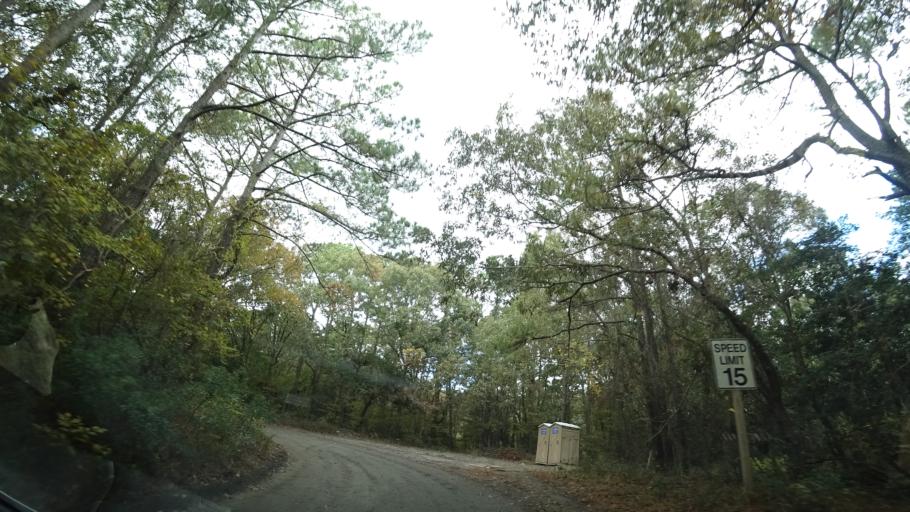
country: US
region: North Carolina
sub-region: Dare County
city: Kill Devil Hills
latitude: 35.9997
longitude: -75.6647
